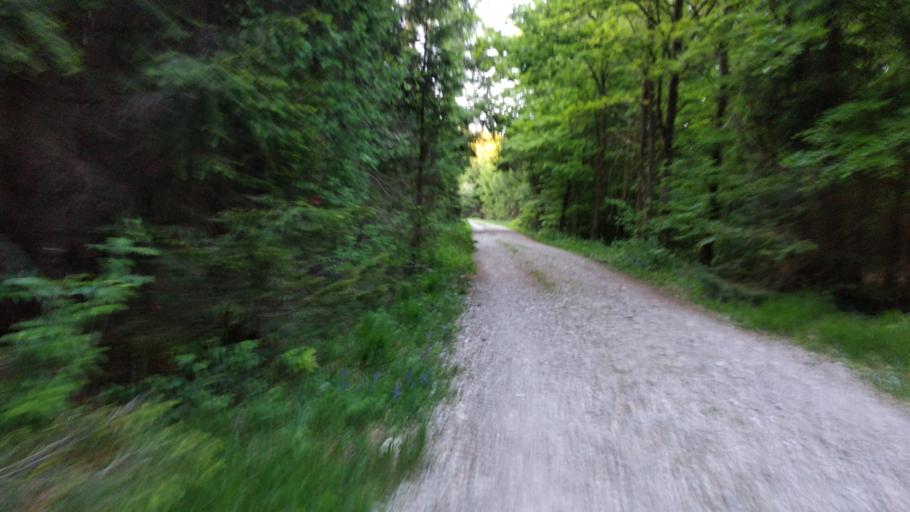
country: DE
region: Bavaria
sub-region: Upper Bavaria
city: Vaterstetten
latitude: 48.0847
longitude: 11.7860
